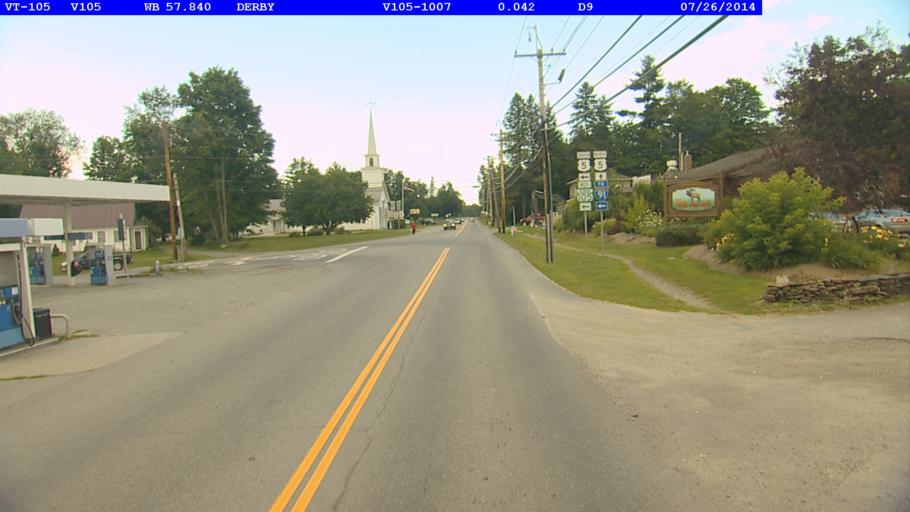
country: US
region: Vermont
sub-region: Orleans County
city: Newport
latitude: 44.9540
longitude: -72.1306
